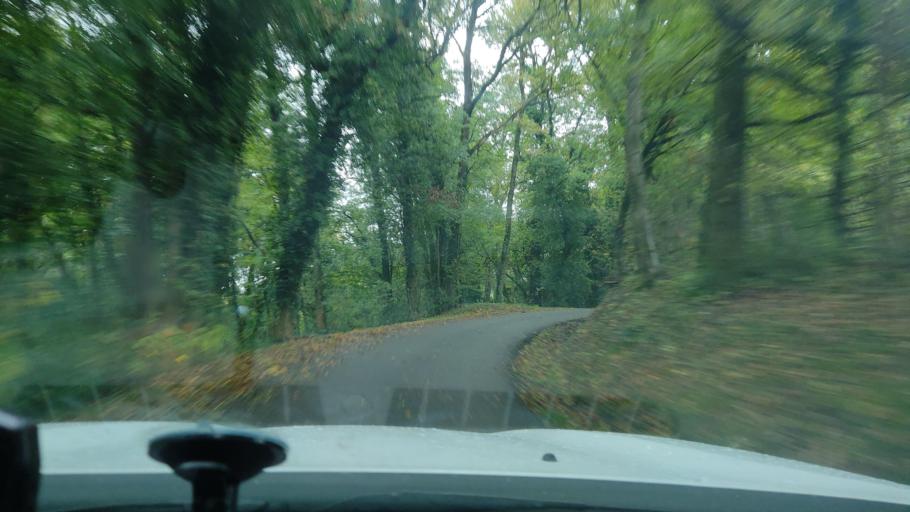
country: FR
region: Rhone-Alpes
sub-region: Departement de la Savoie
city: La Rochette
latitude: 45.4925
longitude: 6.1016
